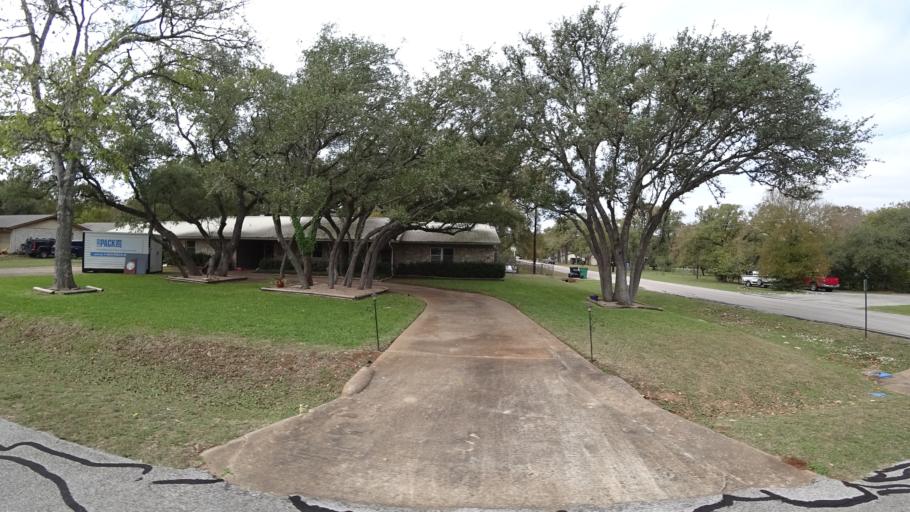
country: US
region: Texas
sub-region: Travis County
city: Shady Hollow
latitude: 30.1389
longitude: -97.8901
